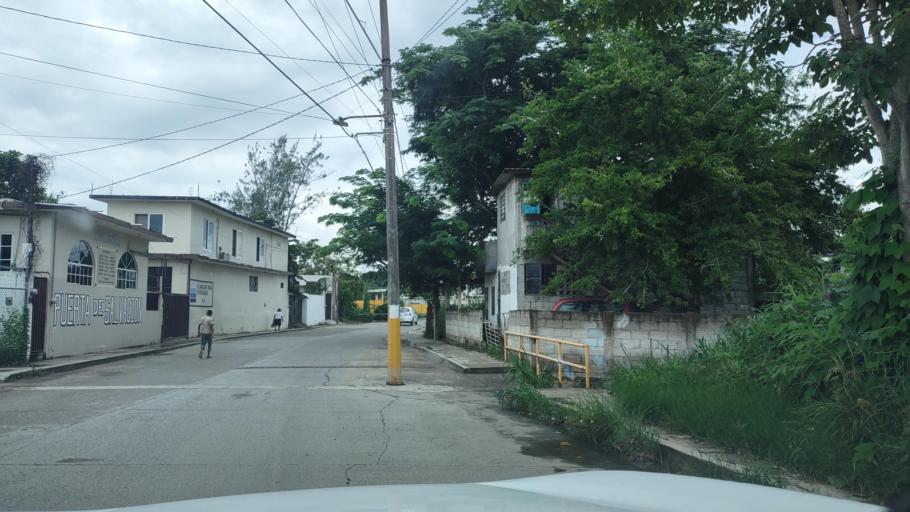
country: MX
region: Veracruz
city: Tuxpan de Rodriguez Cano
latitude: 20.9549
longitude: -97.4218
